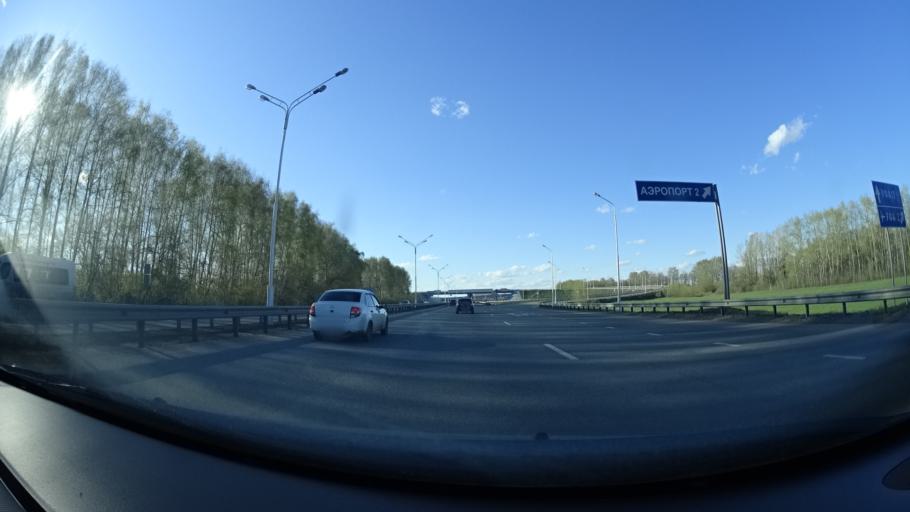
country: RU
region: Bashkortostan
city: Ufa
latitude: 54.5710
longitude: 55.9147
